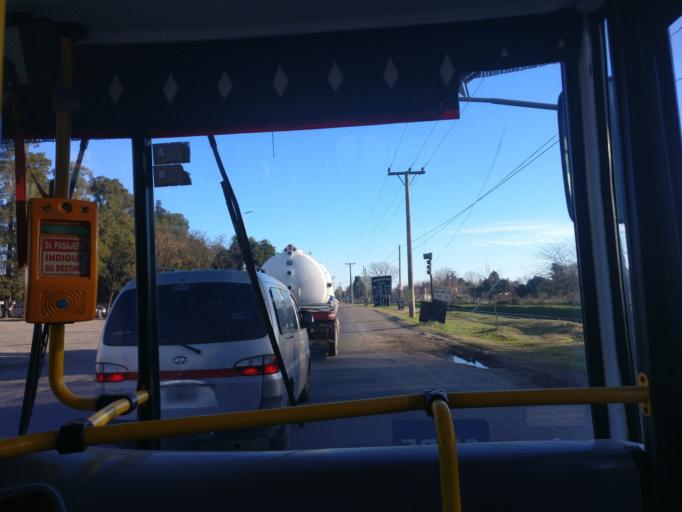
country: AR
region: Buenos Aires
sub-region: Partido de Ezeiza
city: Ezeiza
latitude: -34.9178
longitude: -58.6040
